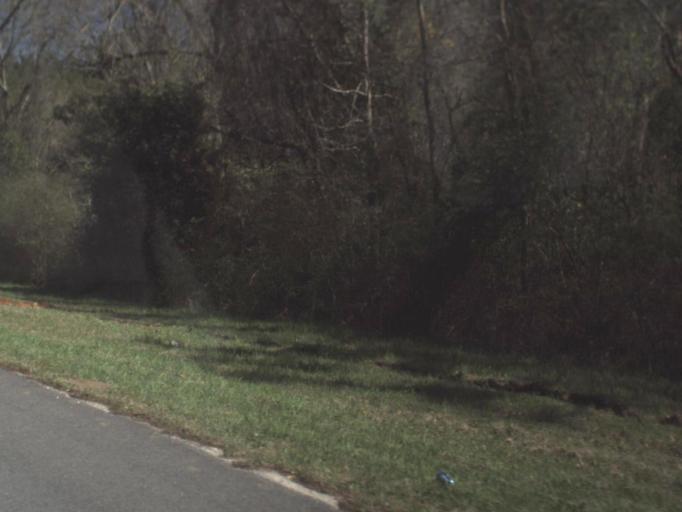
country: US
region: Florida
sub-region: Gadsden County
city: Quincy
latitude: 30.5212
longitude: -84.6072
